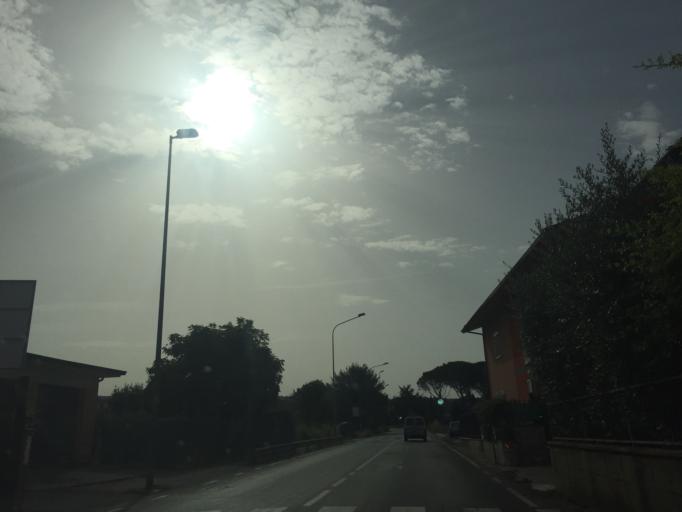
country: IT
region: Tuscany
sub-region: Provincia di Pistoia
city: Monsummano Terme
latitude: 43.8606
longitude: 10.8149
